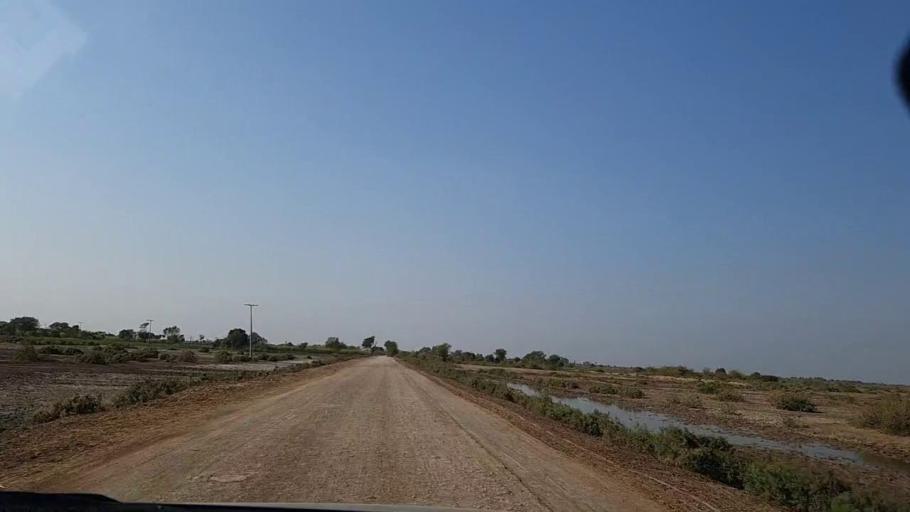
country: PK
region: Sindh
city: Digri
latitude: 25.1892
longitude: 68.9987
